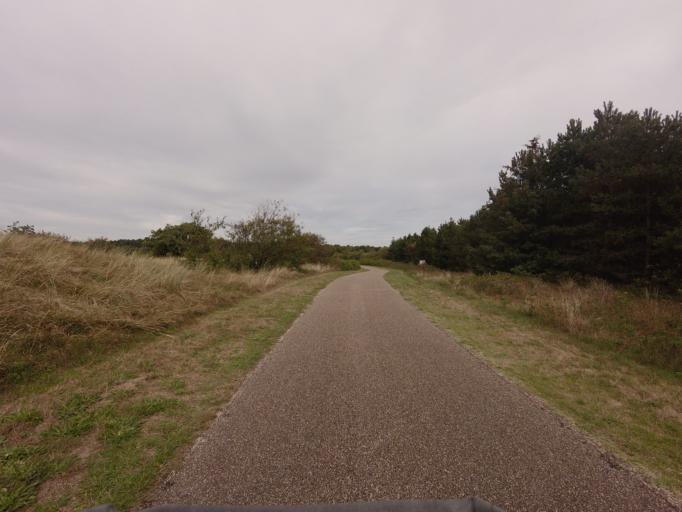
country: NL
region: Friesland
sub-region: Gemeente Ameland
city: Nes
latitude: 53.4505
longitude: 5.7812
